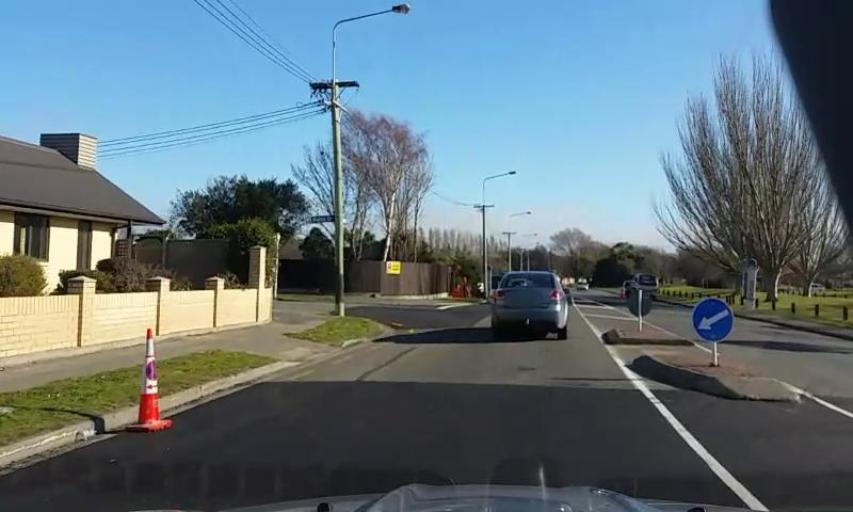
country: NZ
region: Canterbury
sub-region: Christchurch City
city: Christchurch
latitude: -43.4949
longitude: 172.7082
